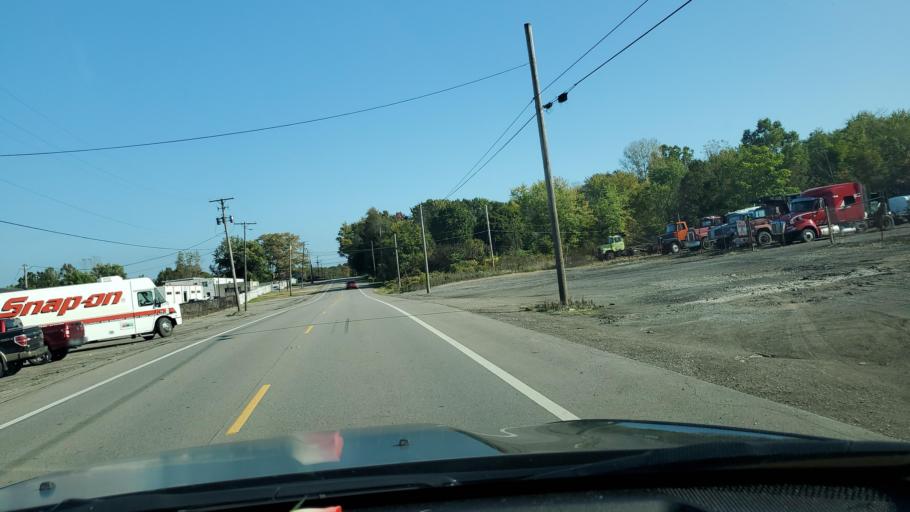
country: US
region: Ohio
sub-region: Mahoning County
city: Youngstown
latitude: 41.1343
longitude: -80.6238
